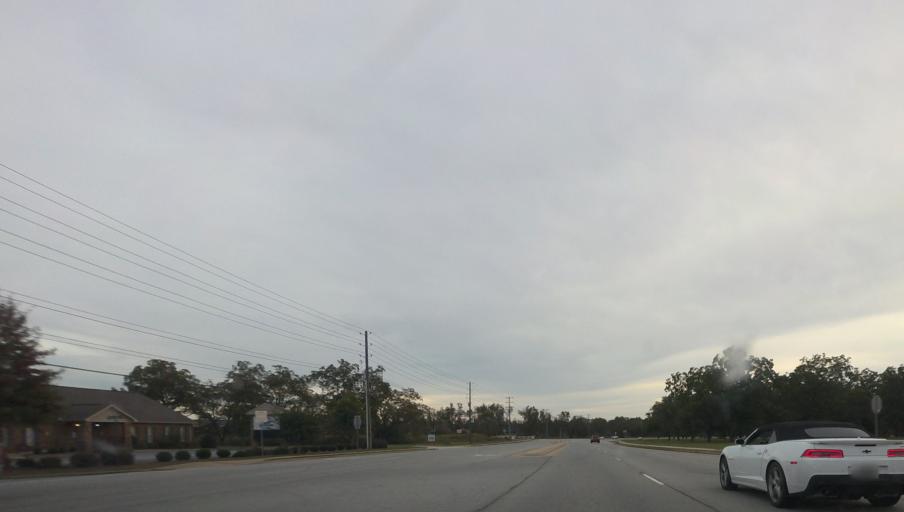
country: US
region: Georgia
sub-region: Houston County
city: Perry
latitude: 32.5039
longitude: -83.6627
